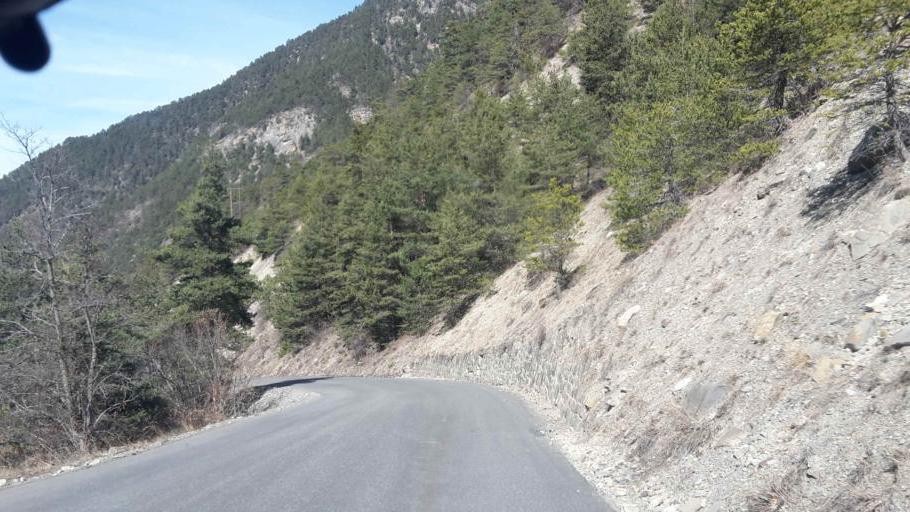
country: FR
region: Provence-Alpes-Cote d'Azur
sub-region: Departement des Hautes-Alpes
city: Embrun
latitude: 44.5525
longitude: 6.5775
